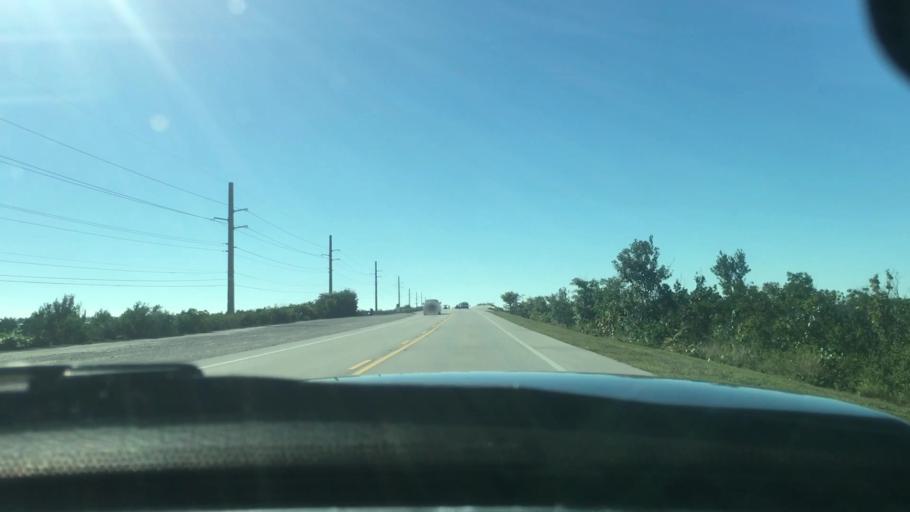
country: US
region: Florida
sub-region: Monroe County
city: Cudjoe Key
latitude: 24.6555
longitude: -81.5383
